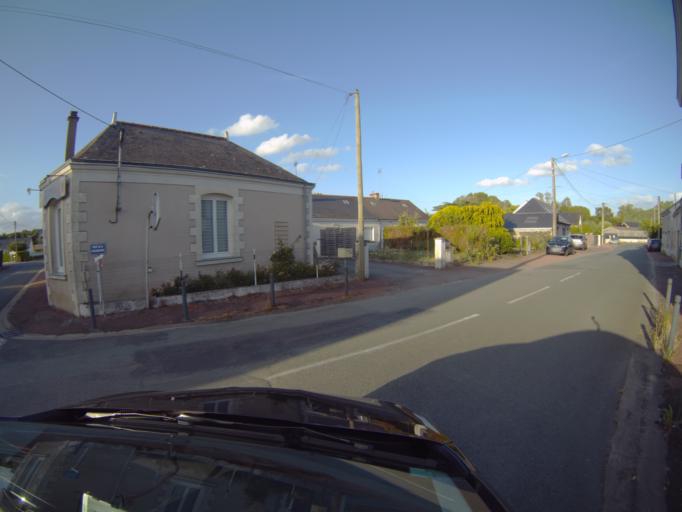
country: FR
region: Pays de la Loire
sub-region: Departement de Maine-et-Loire
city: Andard
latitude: 47.4687
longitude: -0.4074
